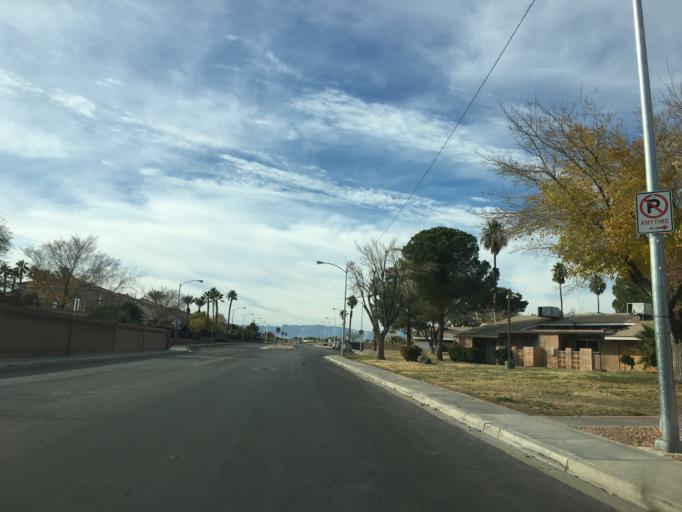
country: US
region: Nevada
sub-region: Clark County
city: Enterprise
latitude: 36.0173
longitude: -115.1682
